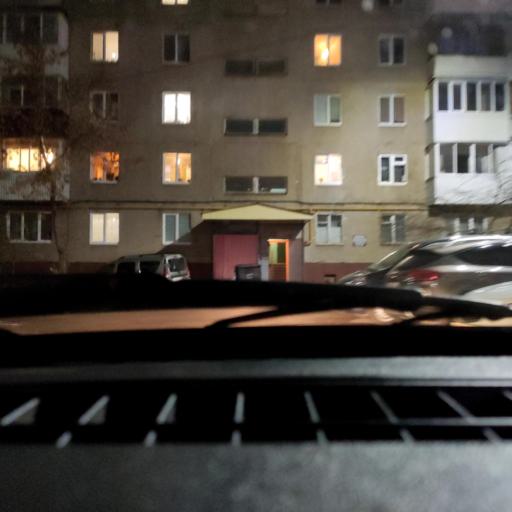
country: RU
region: Bashkortostan
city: Ufa
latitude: 54.8193
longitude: 56.1289
